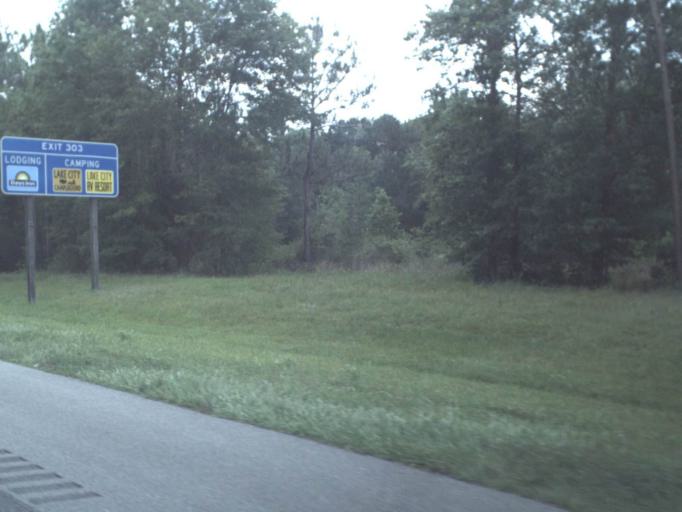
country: US
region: Florida
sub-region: Columbia County
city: Five Points
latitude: 30.2436
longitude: -82.6577
